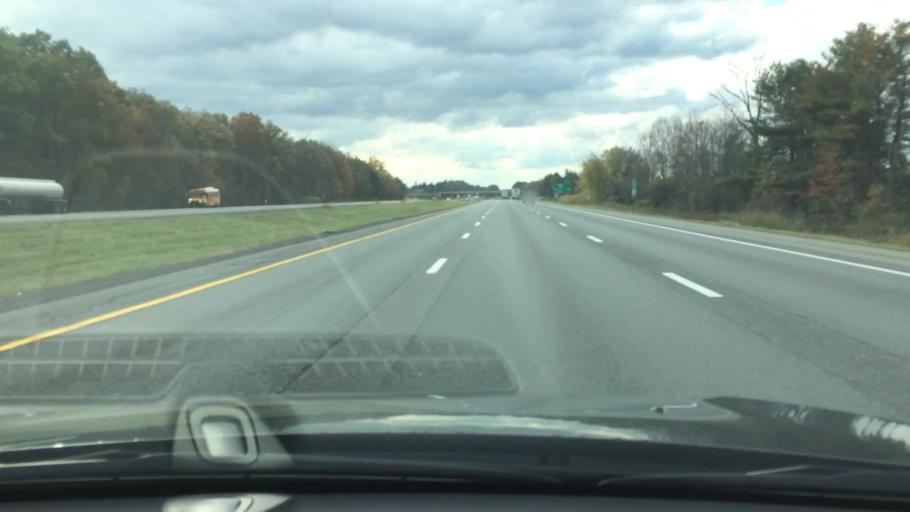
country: US
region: New York
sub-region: Saratoga County
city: Ballston Spa
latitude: 42.9778
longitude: -73.8028
